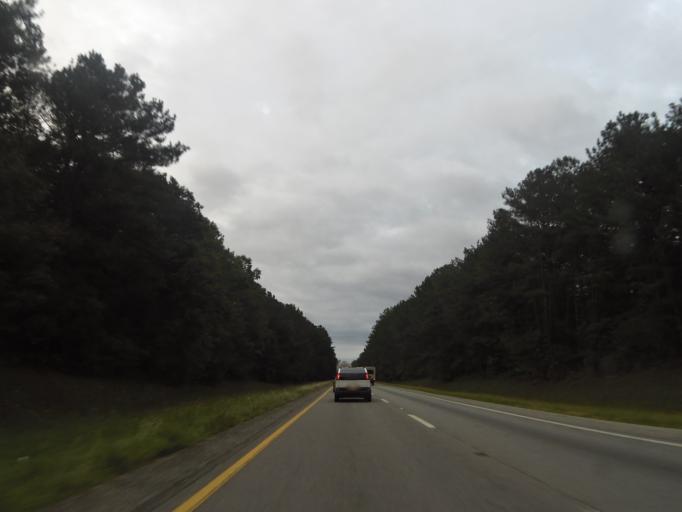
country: US
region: Alabama
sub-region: Saint Clair County
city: Springville
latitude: 33.7960
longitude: -86.3781
